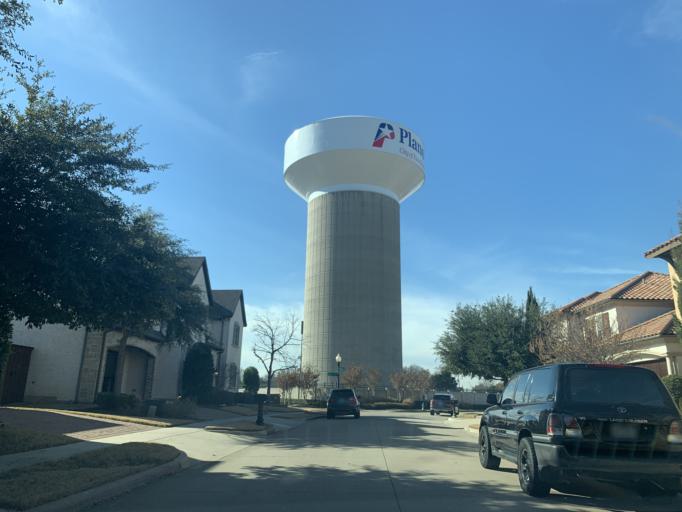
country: US
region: Texas
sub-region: Denton County
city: The Colony
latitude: 33.0576
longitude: -96.8205
